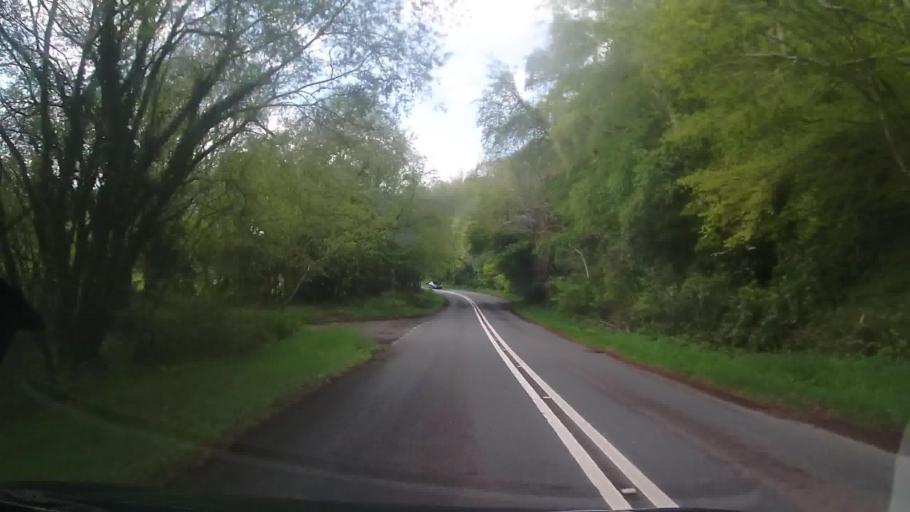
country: GB
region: Wales
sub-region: Gwynedd
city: Porthmadog
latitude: 52.9425
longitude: -4.1314
